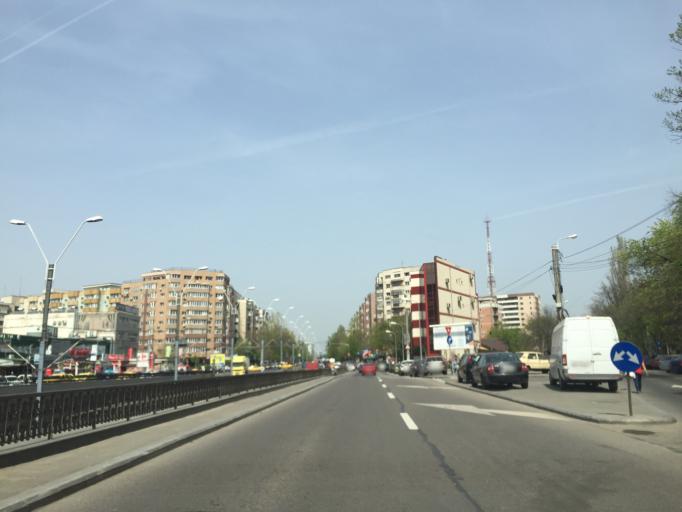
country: RO
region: Ilfov
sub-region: Comuna Chiajna
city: Rosu
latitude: 44.4349
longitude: 26.0352
